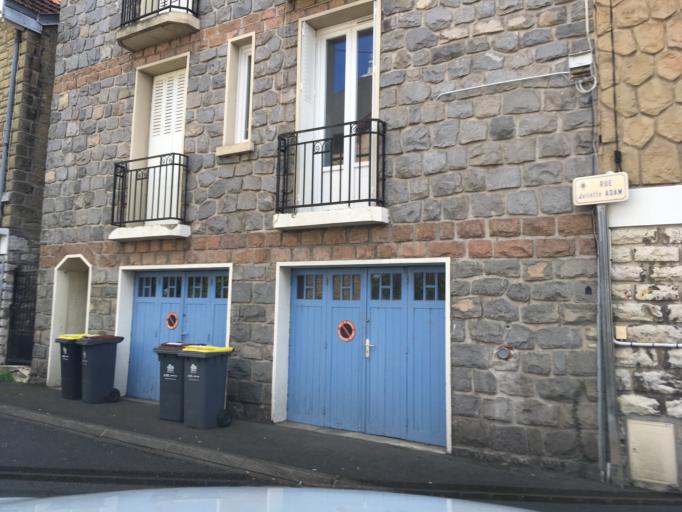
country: FR
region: Limousin
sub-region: Departement de la Correze
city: Brive-la-Gaillarde
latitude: 45.1549
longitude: 1.5248
